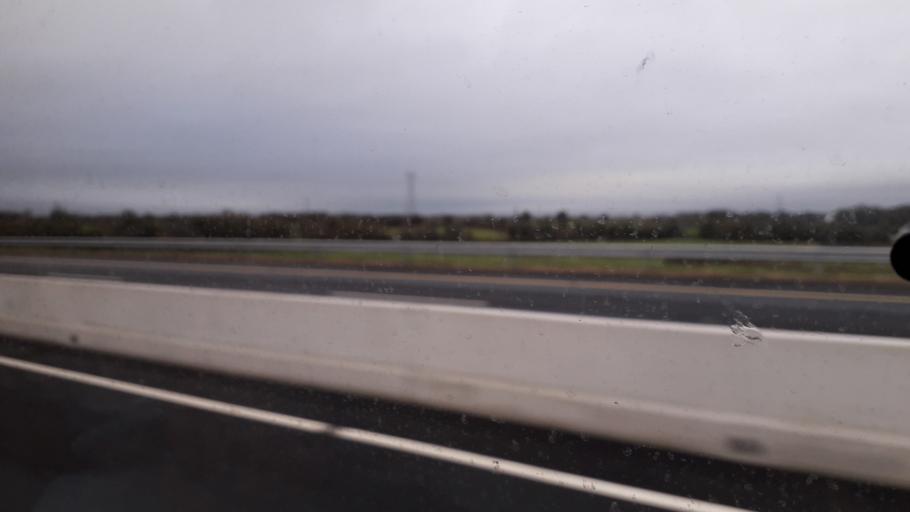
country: IE
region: Connaught
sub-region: County Galway
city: Athenry
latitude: 53.2846
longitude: -8.8036
